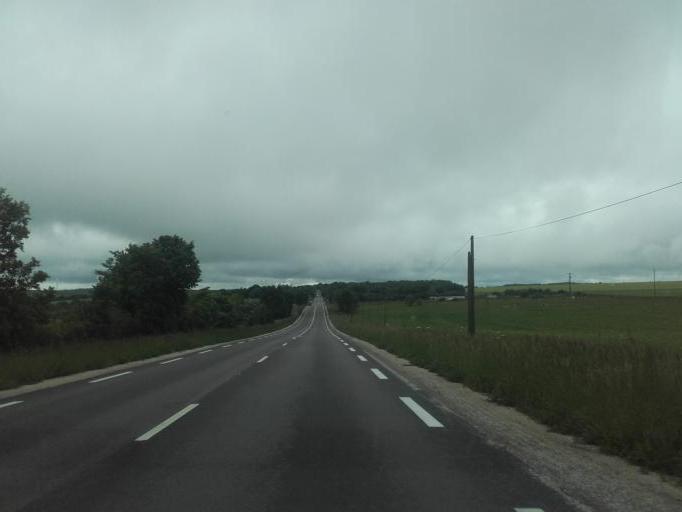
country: FR
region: Bourgogne
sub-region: Departement de la Cote-d'Or
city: Nolay
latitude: 46.9842
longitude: 4.6707
